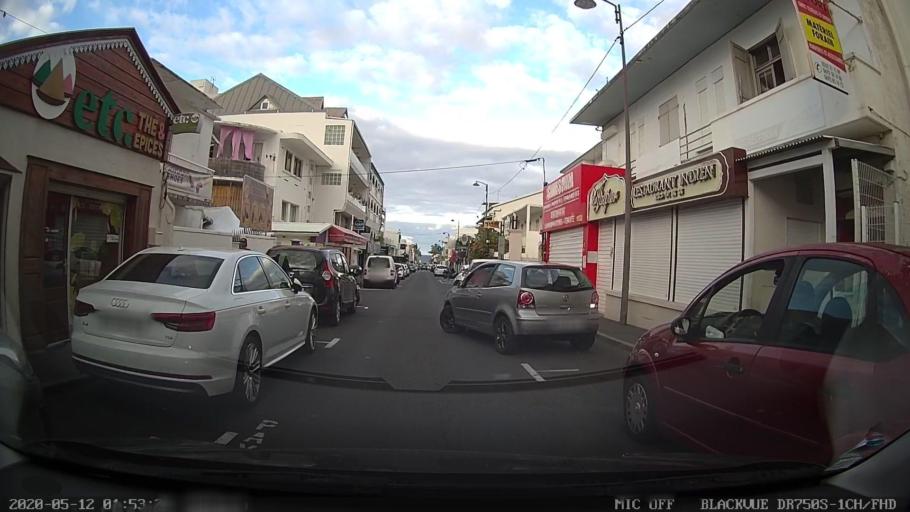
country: RE
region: Reunion
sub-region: Reunion
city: Saint-Denis
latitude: -20.8786
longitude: 55.4515
